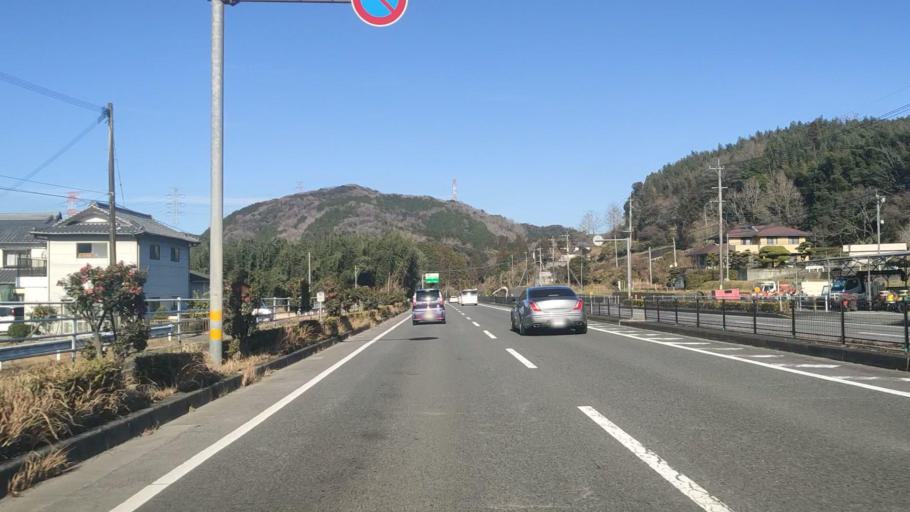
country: JP
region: Oita
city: Oita
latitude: 33.1060
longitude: 131.6544
